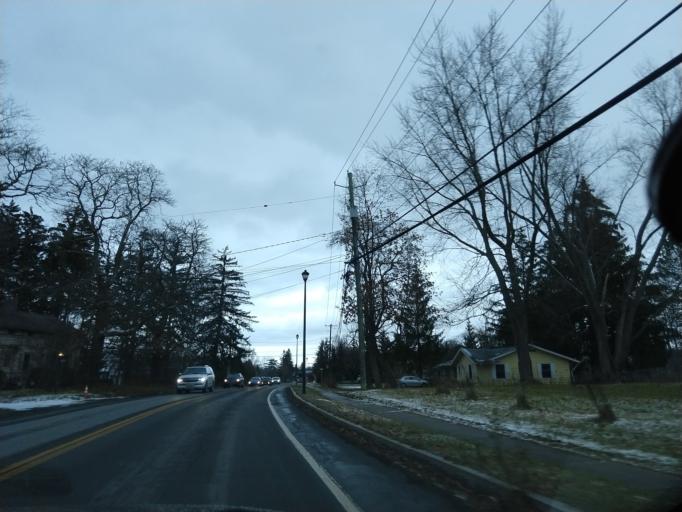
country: US
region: New York
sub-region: Tompkins County
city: Lansing
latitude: 42.4717
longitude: -76.4811
